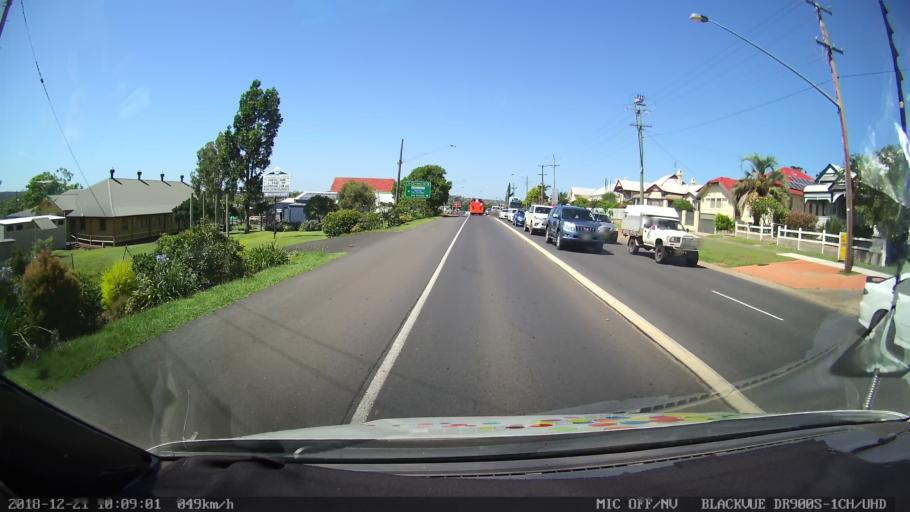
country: AU
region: New South Wales
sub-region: Clarence Valley
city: Grafton
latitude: -29.7019
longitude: 152.9416
